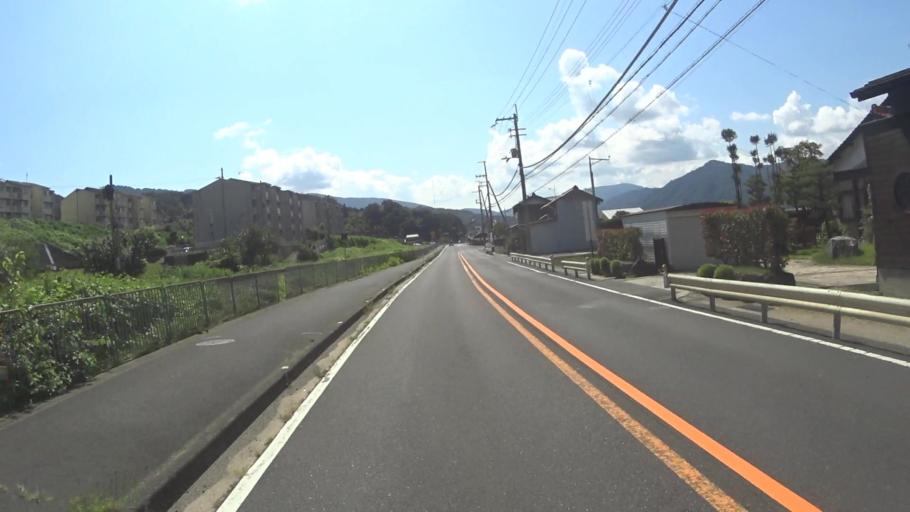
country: JP
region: Kyoto
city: Miyazu
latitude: 35.5439
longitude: 135.2102
